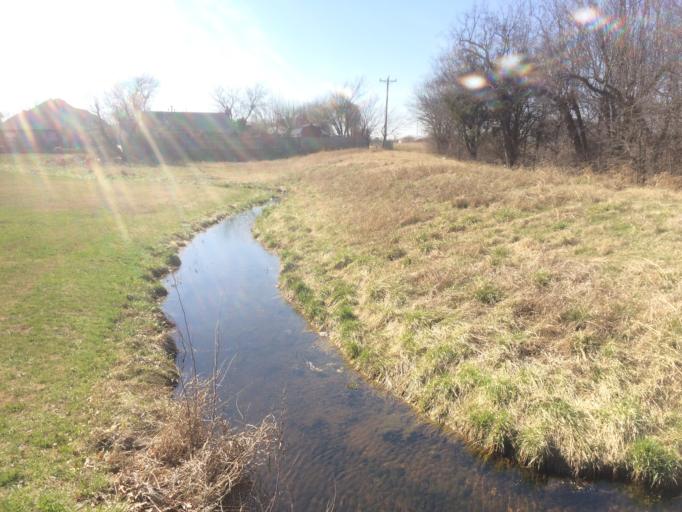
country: US
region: Oklahoma
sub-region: Cleveland County
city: Norman
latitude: 35.2400
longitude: -97.4372
